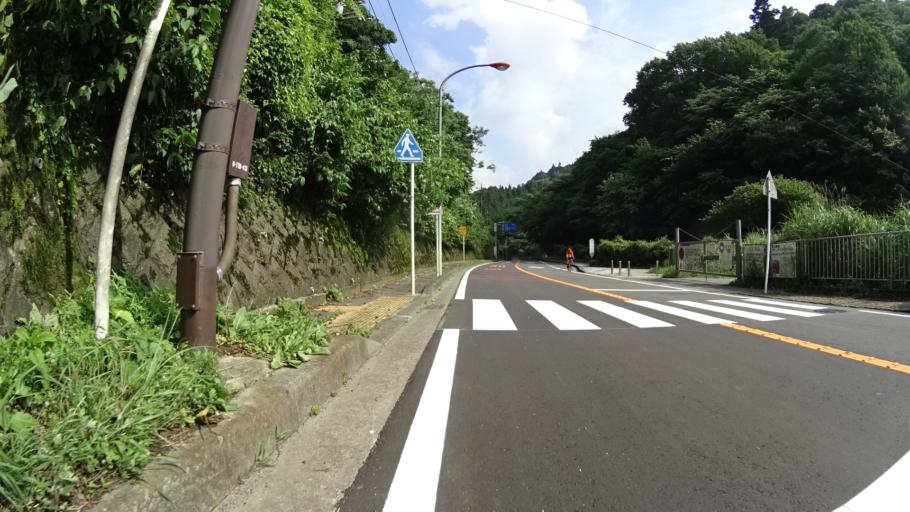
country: JP
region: Kanagawa
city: Atsugi
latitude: 35.5041
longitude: 139.2564
